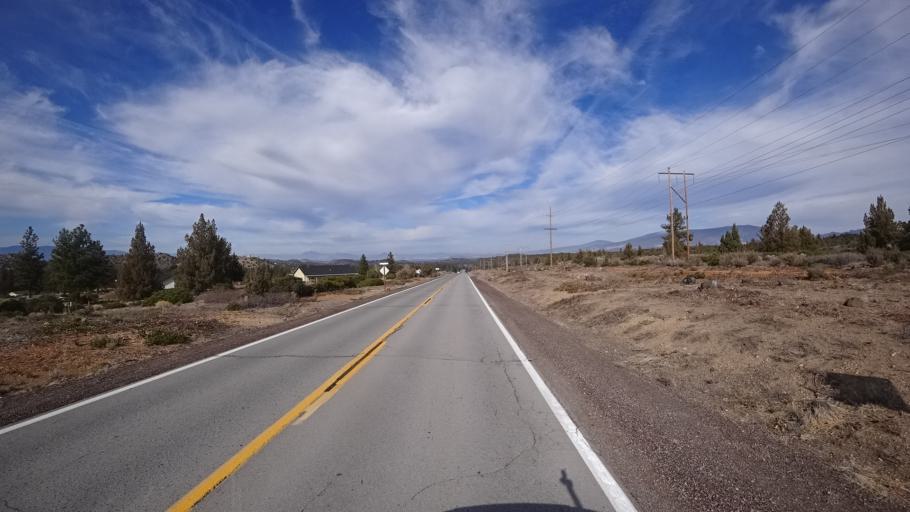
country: US
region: California
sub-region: Siskiyou County
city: Weed
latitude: 41.4956
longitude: -122.3626
